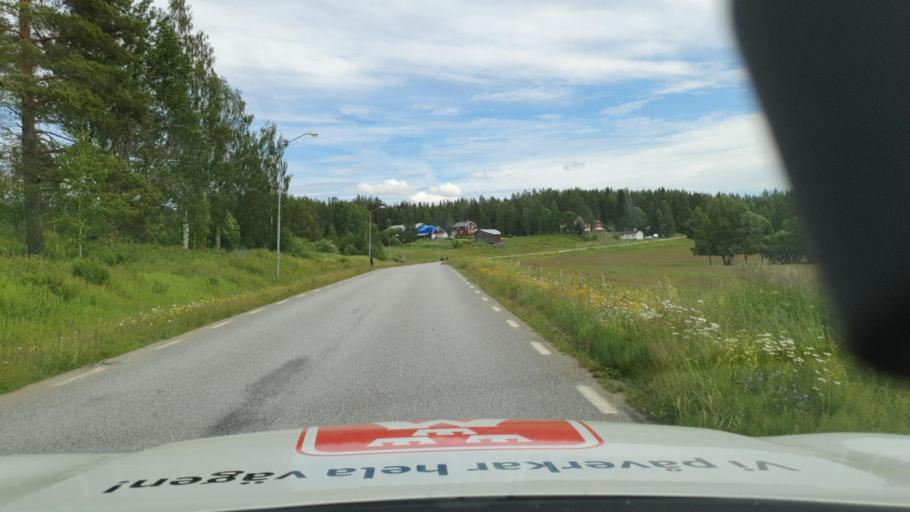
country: SE
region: Vaesterbotten
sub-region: Skelleftea Kommun
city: Burea
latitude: 64.4914
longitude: 21.0288
